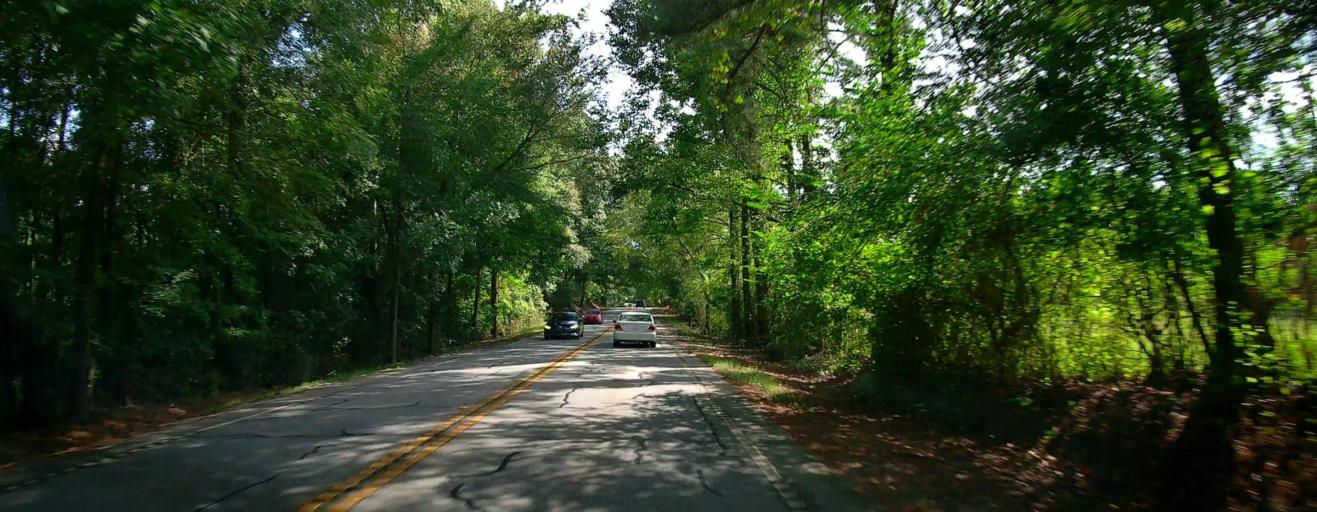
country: US
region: Georgia
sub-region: Harris County
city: Hamilton
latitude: 32.6816
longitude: -84.8582
